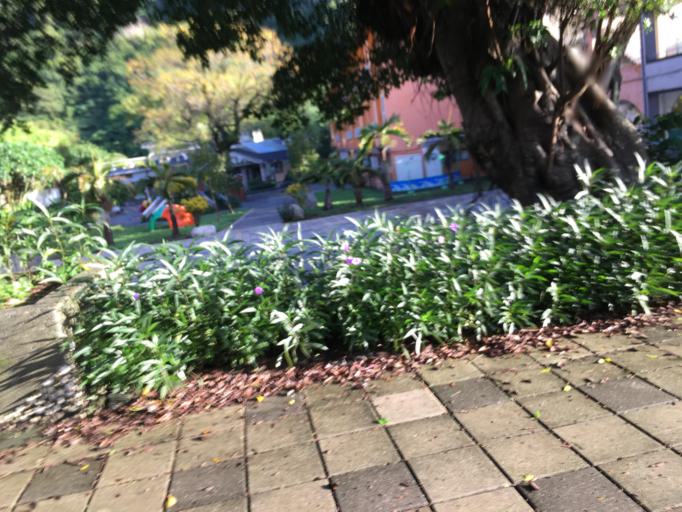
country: TW
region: Taiwan
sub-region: Yilan
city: Yilan
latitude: 24.5963
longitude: 121.8401
